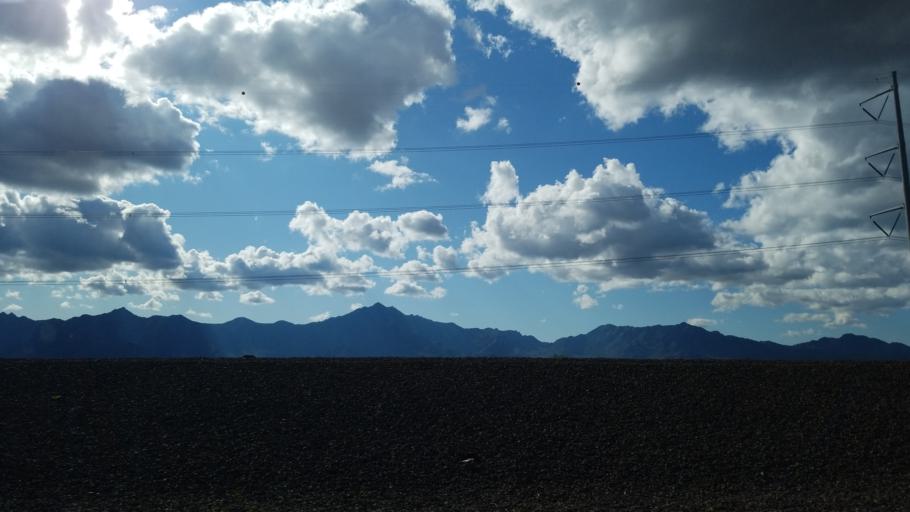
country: US
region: Arizona
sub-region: Maricopa County
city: Laveen
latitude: 33.3459
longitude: -112.1889
